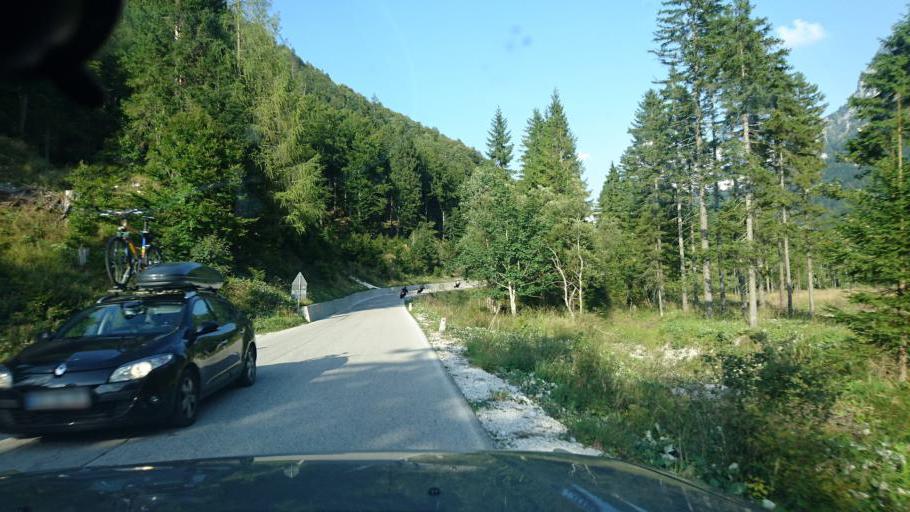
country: SI
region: Bovec
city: Bovec
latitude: 46.4032
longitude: 13.5211
